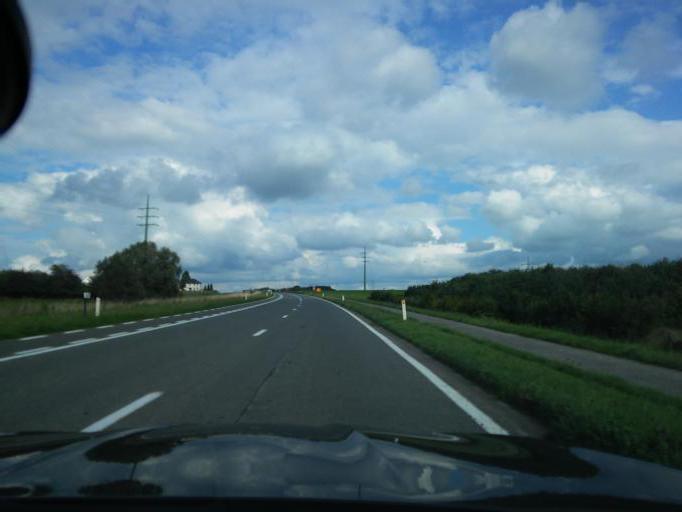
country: BE
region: Flanders
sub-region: Provincie Vlaams-Brabant
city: Galmaarden
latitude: 50.8147
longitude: 3.9497
